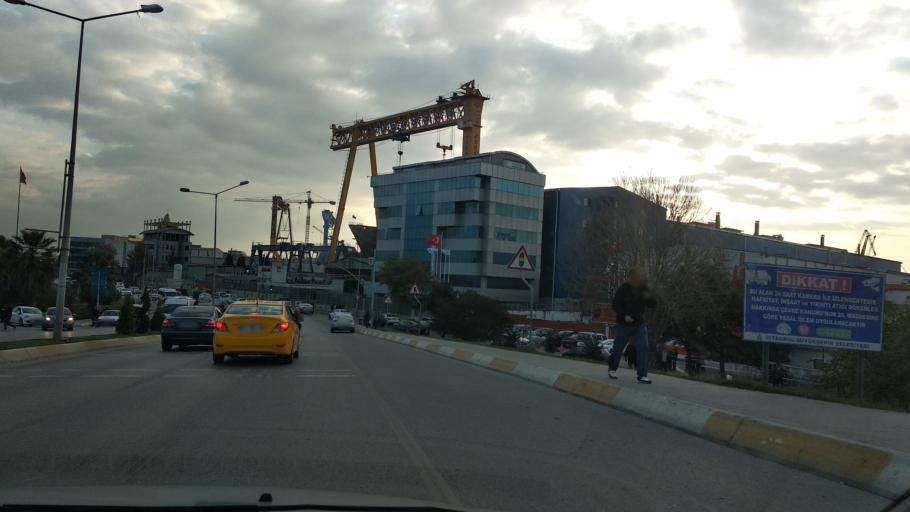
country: TR
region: Istanbul
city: Icmeler
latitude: 40.8468
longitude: 29.2941
